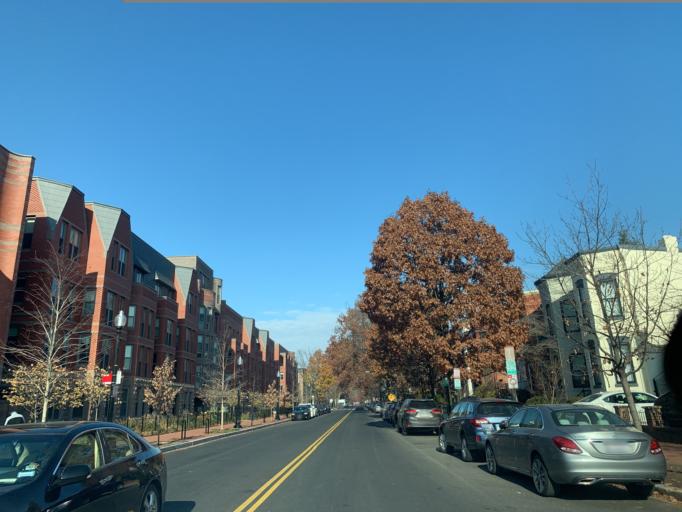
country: US
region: Washington, D.C.
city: Washington, D.C.
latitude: 38.8846
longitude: -76.9949
